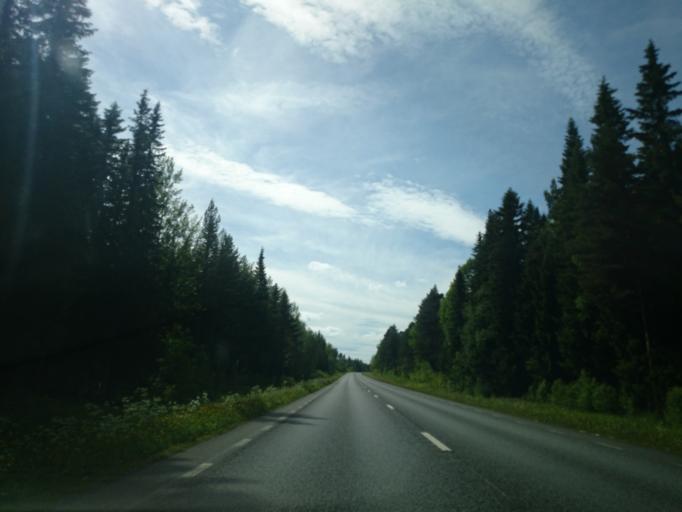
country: SE
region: Jaemtland
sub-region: Krokoms Kommun
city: Krokom
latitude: 63.3135
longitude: 14.1432
